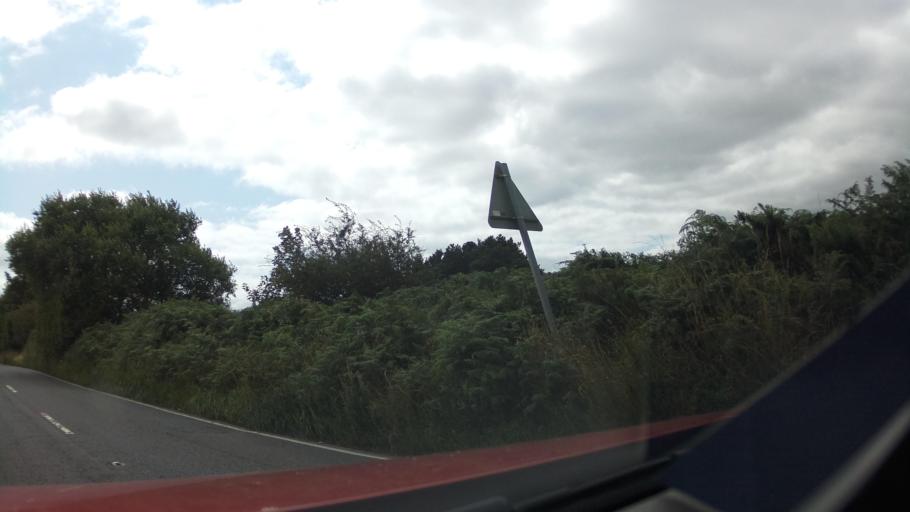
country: GB
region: England
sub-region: Devon
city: Bishopsteignton
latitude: 50.5757
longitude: -3.5275
